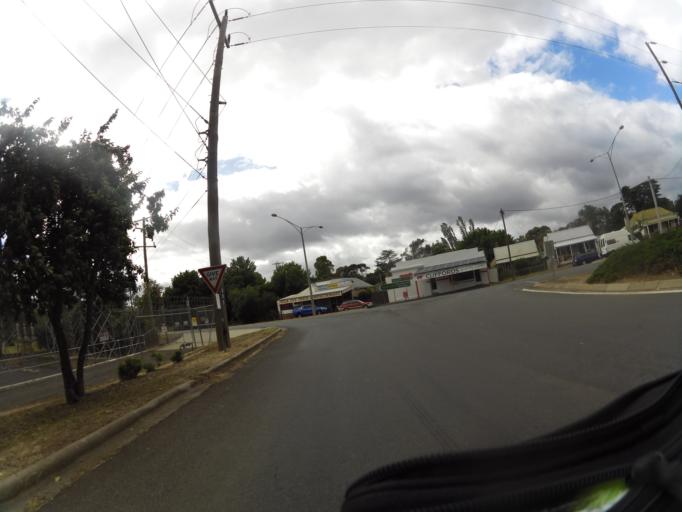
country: AU
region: Victoria
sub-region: Mount Alexander
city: Castlemaine
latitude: -37.0727
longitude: 144.2066
